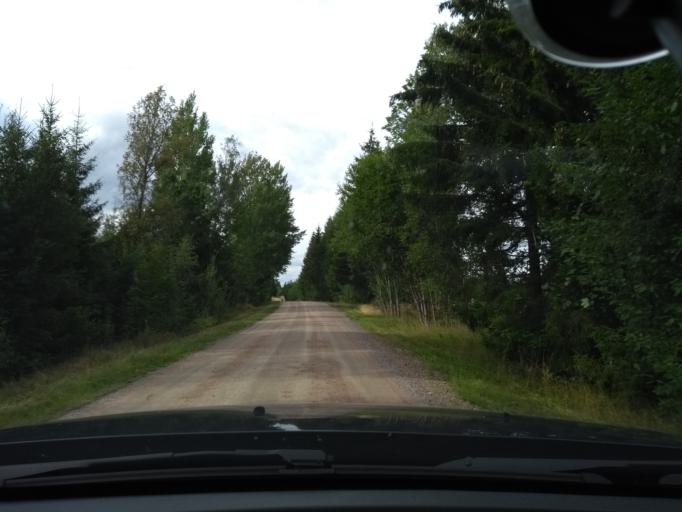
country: SE
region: Joenkoeping
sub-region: Eksjo Kommun
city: Mariannelund
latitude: 57.6276
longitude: 15.6408
